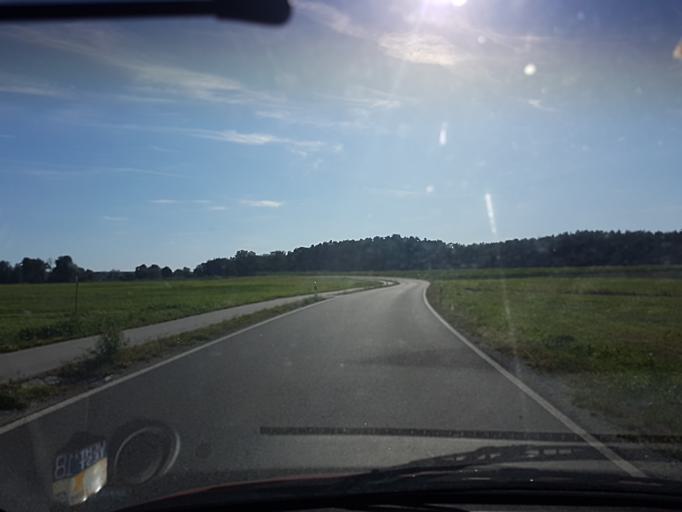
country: DE
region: Bavaria
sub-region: Upper Franconia
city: Hallerndorf
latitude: 49.7429
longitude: 10.9543
